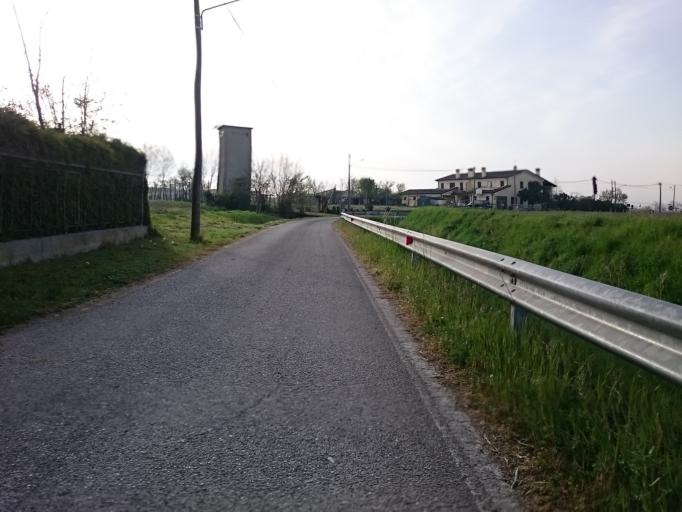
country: IT
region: Veneto
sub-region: Provincia di Padova
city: Albignasego
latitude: 45.3654
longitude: 11.8823
